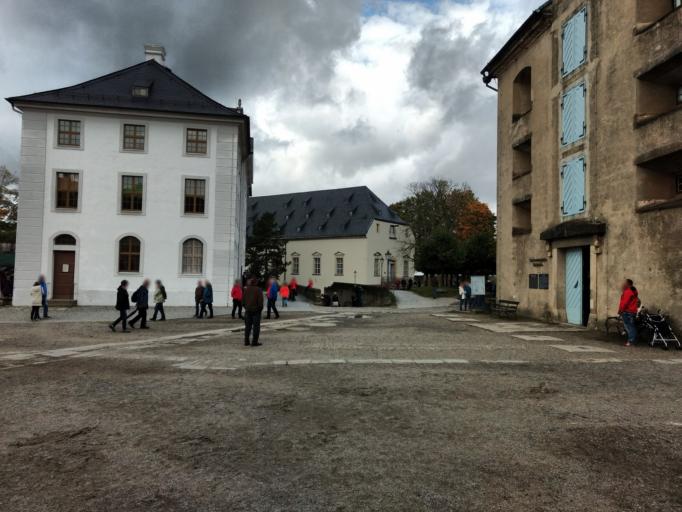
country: DE
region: Saxony
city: Konigstein
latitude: 50.9189
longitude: 14.0574
